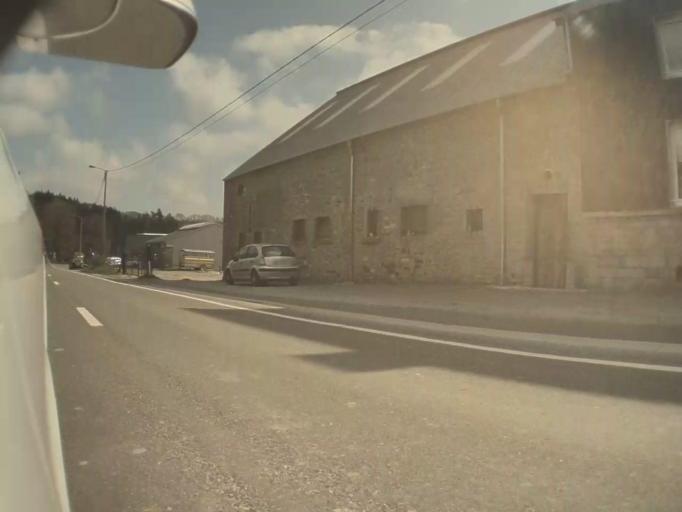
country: BE
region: Wallonia
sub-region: Province du Luxembourg
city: Tellin
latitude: 50.0872
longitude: 5.2242
